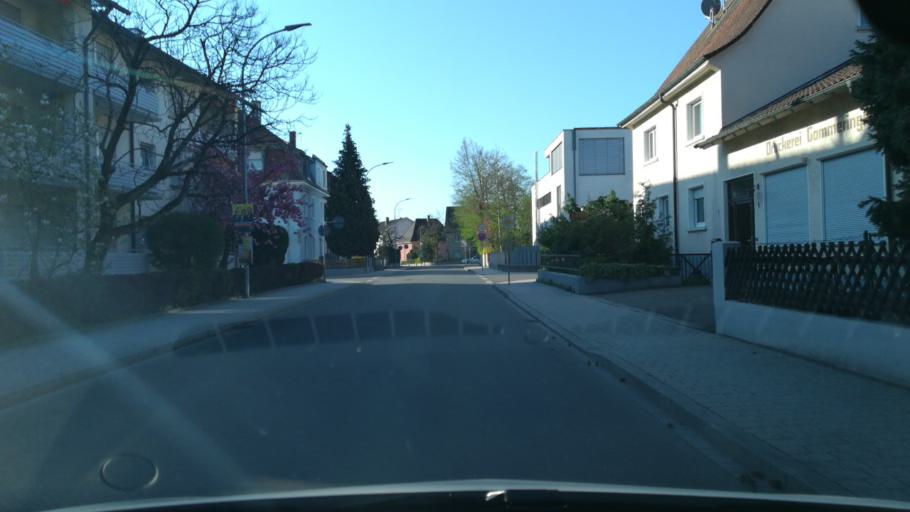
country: DE
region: Baden-Wuerttemberg
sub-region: Freiburg Region
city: Singen
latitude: 47.7676
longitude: 8.8411
